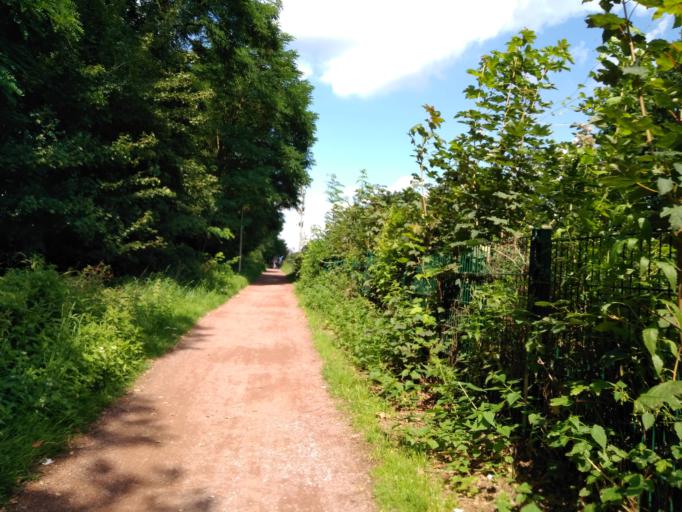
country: DE
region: North Rhine-Westphalia
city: Dorsten
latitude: 51.6648
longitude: 6.9710
